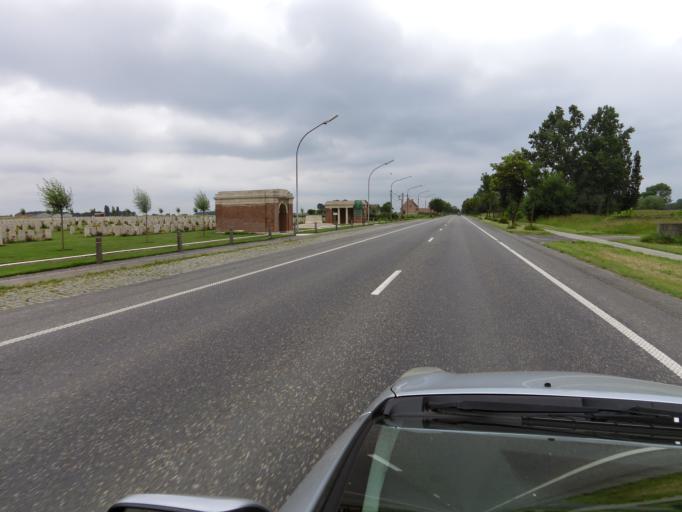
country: BE
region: Flanders
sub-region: Provincie West-Vlaanderen
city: Ieper
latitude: 50.8761
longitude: 2.8695
